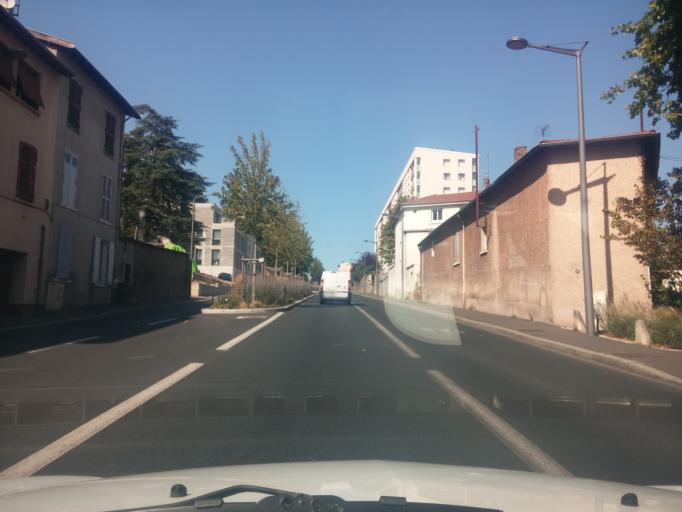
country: FR
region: Rhone-Alpes
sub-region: Departement du Rhone
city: Oullins
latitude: 45.7188
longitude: 4.8103
